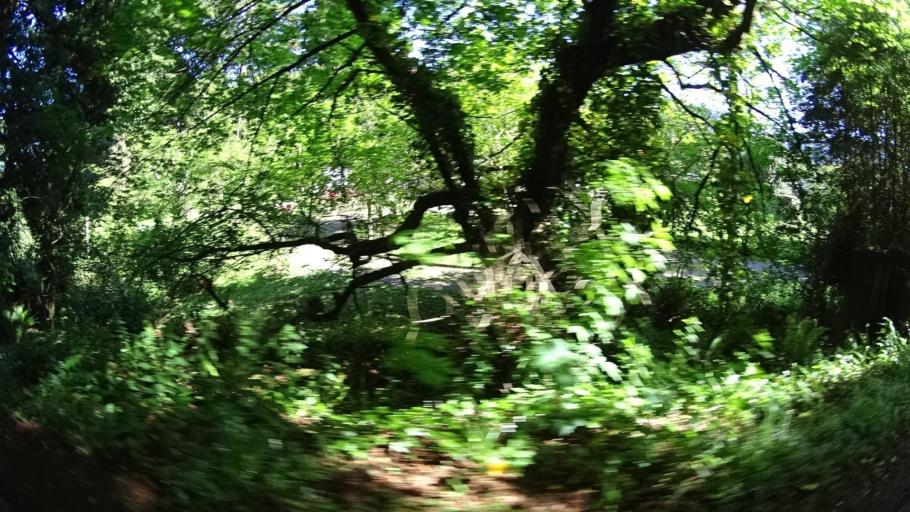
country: US
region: California
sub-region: Humboldt County
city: Rio Dell
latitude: 40.5071
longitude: -124.1247
